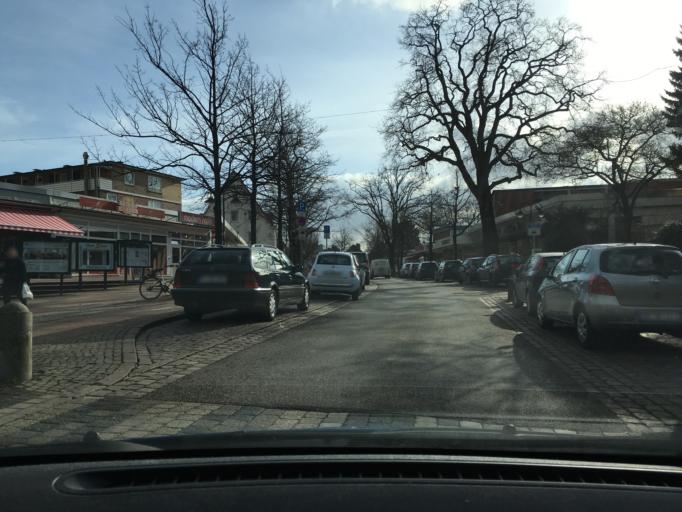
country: DE
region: Schleswig-Holstein
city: Wedel
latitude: 53.5805
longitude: 9.7035
